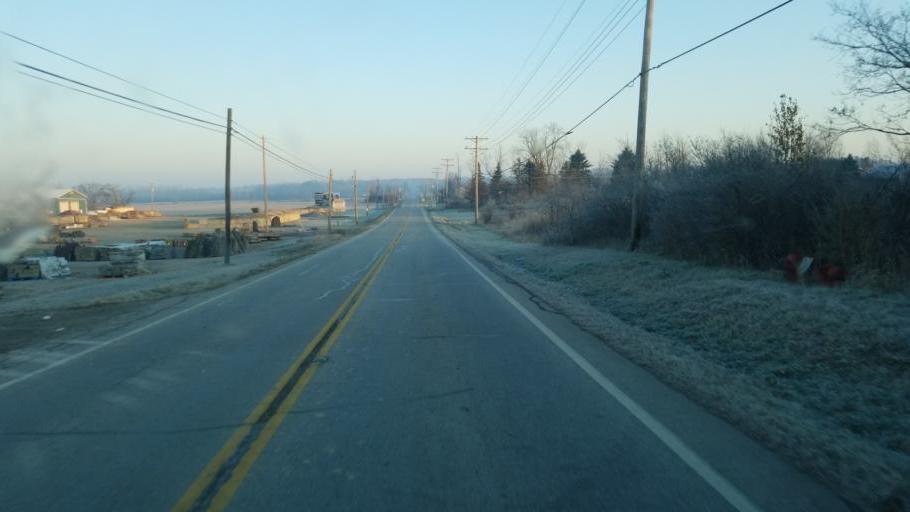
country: US
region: Ohio
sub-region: Medina County
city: Lodi
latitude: 41.0074
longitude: -81.9962
